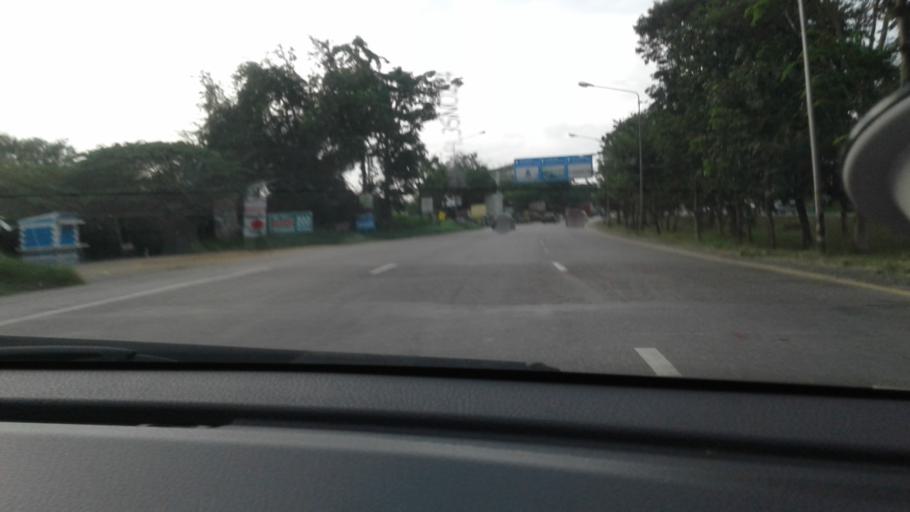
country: TH
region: Prachuap Khiri Khan
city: Pran Buri
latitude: 12.4208
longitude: 99.9238
